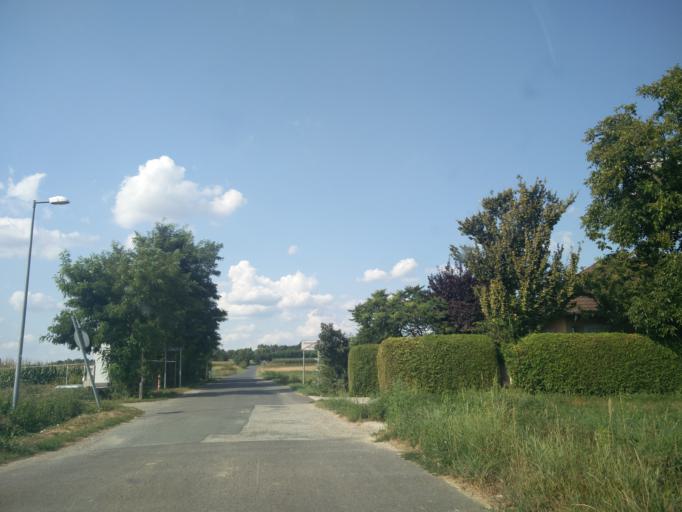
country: HU
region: Zala
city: Zalaegerszeg
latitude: 46.8909
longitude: 16.7931
